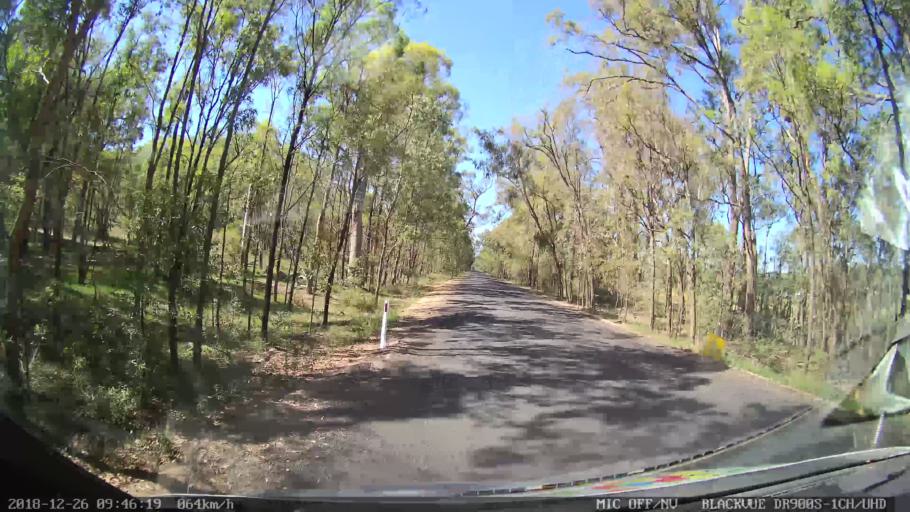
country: AU
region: New South Wales
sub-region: Mid-Western Regional
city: Kandos
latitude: -32.9687
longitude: 150.1055
